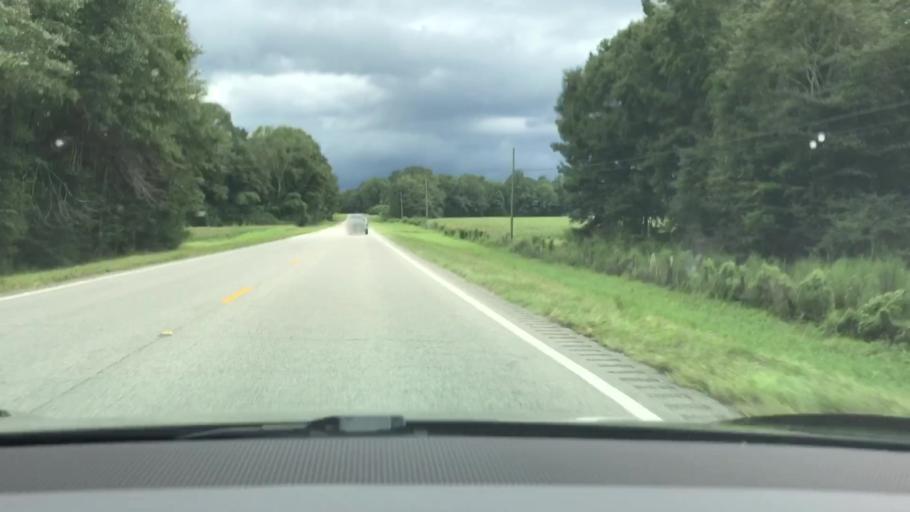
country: US
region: Alabama
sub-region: Coffee County
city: Elba
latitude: 31.5068
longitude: -86.0507
